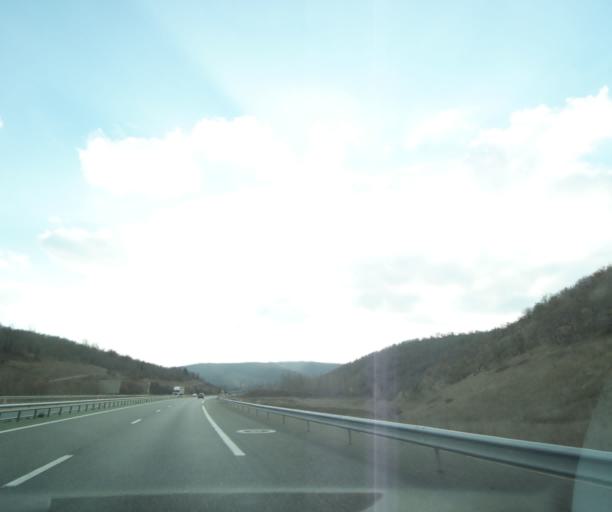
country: FR
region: Midi-Pyrenees
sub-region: Departement du Lot
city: Cahors
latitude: 44.4737
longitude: 1.5050
